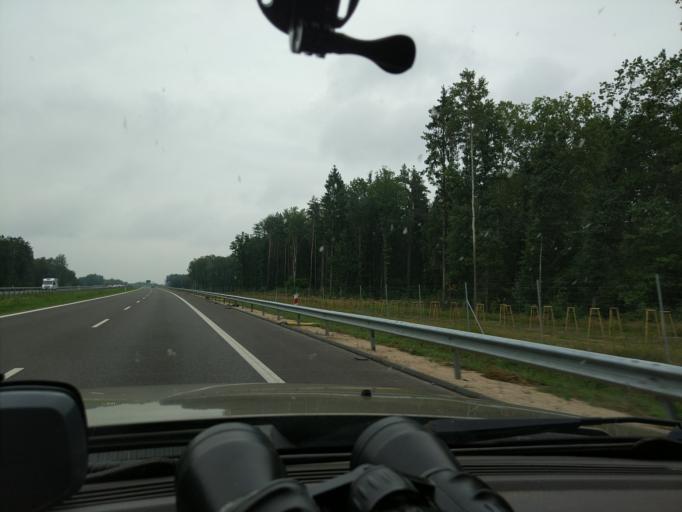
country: PL
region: Podlasie
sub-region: Powiat zambrowski
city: Szumowo
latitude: 52.9325
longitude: 22.1381
